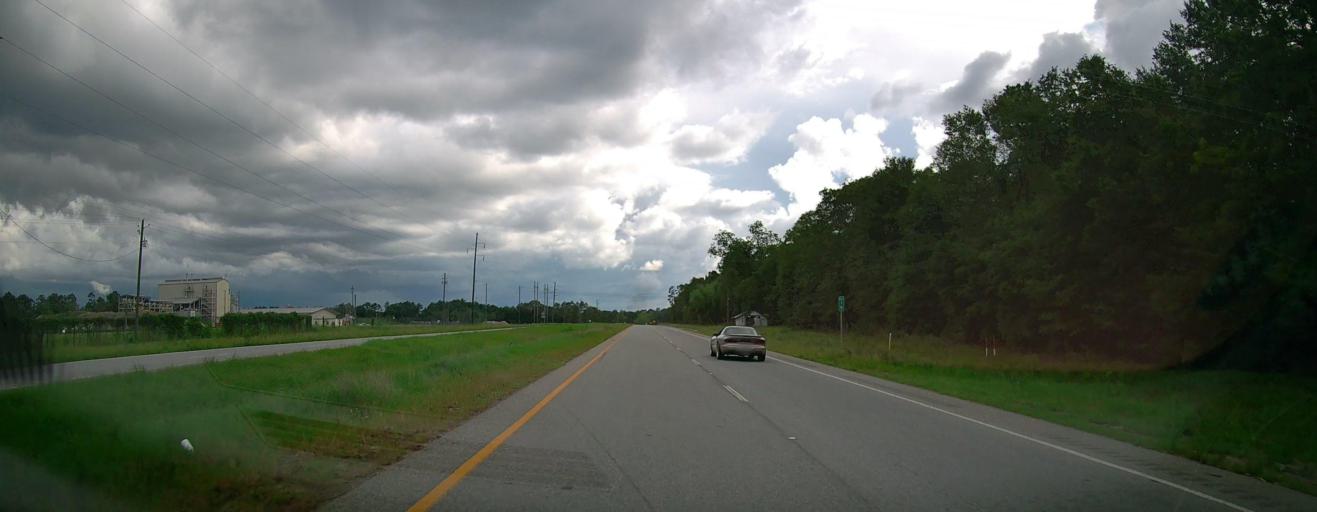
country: US
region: Georgia
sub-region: Pierce County
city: Blackshear
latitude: 31.4186
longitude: -82.1023
